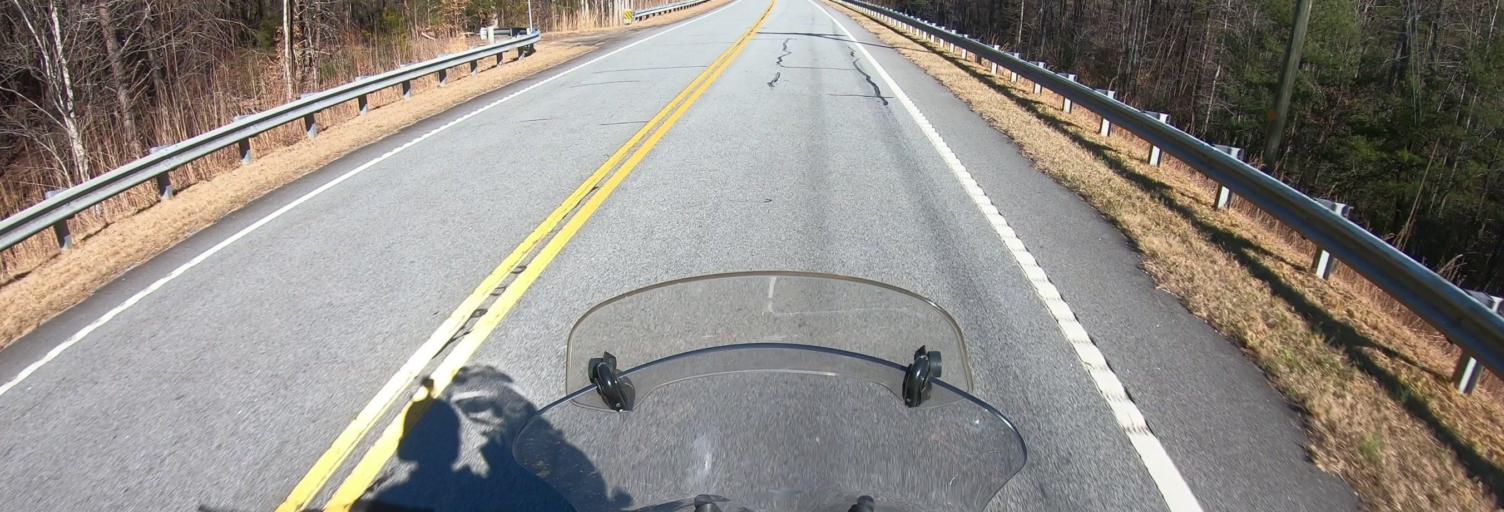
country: US
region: South Carolina
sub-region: Pickens County
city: Pickens
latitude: 34.9623
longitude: -82.8263
